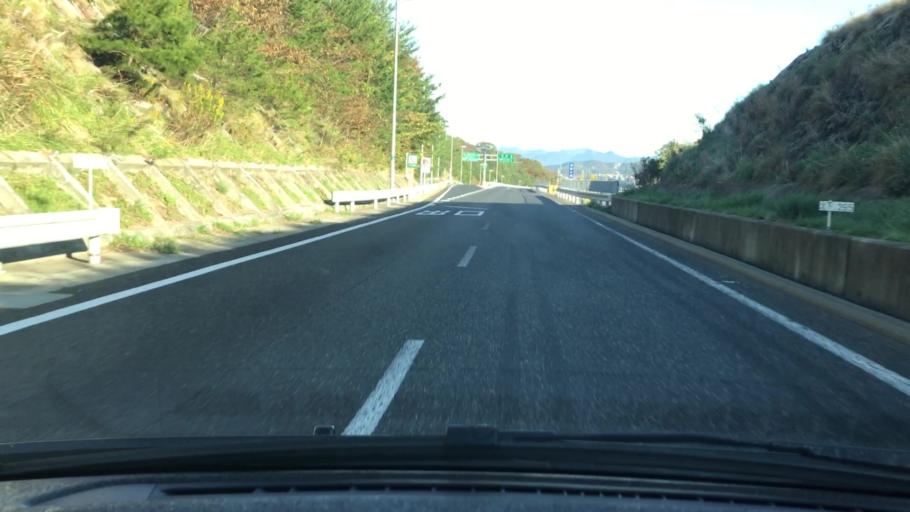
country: JP
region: Hyogo
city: Sandacho
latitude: 34.8123
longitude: 135.2471
